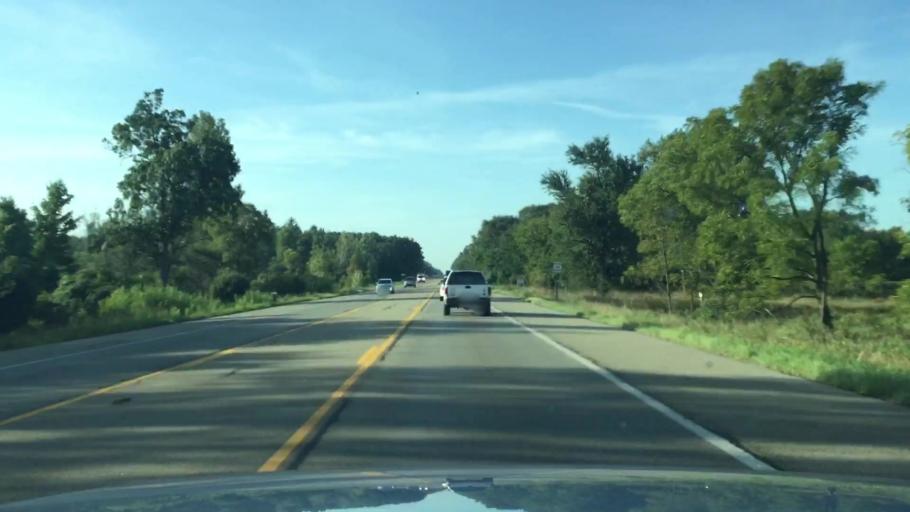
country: US
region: Michigan
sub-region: Jackson County
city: Vandercook Lake
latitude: 42.1749
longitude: -84.3647
